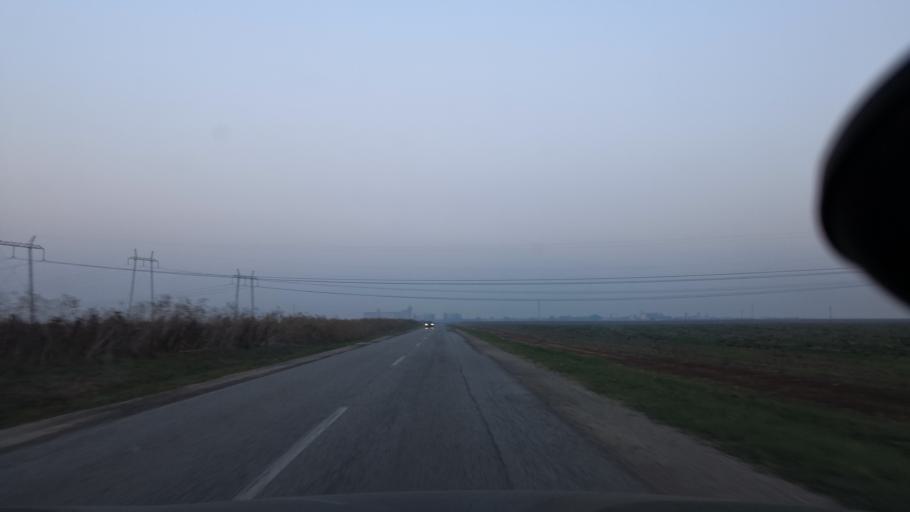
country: RS
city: Golubinci
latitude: 44.9818
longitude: 20.1114
